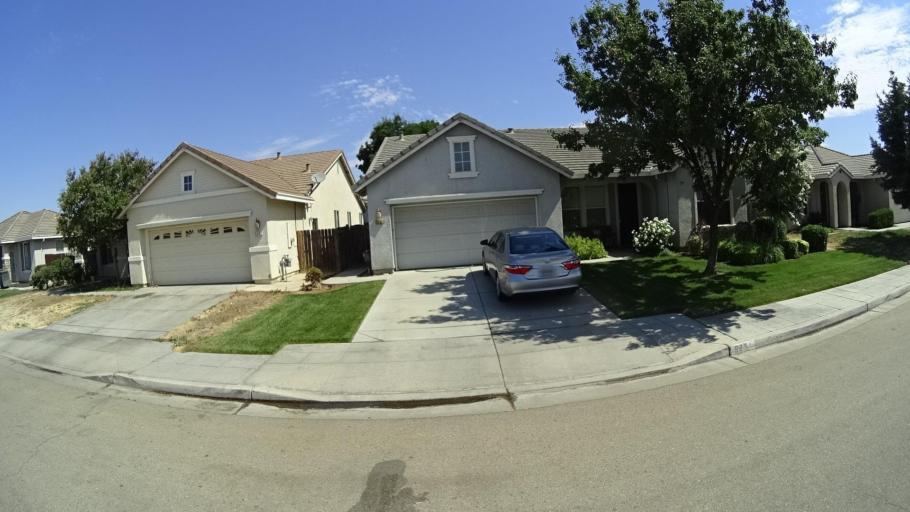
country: US
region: California
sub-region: Fresno County
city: Sunnyside
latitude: 36.7098
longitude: -119.7158
